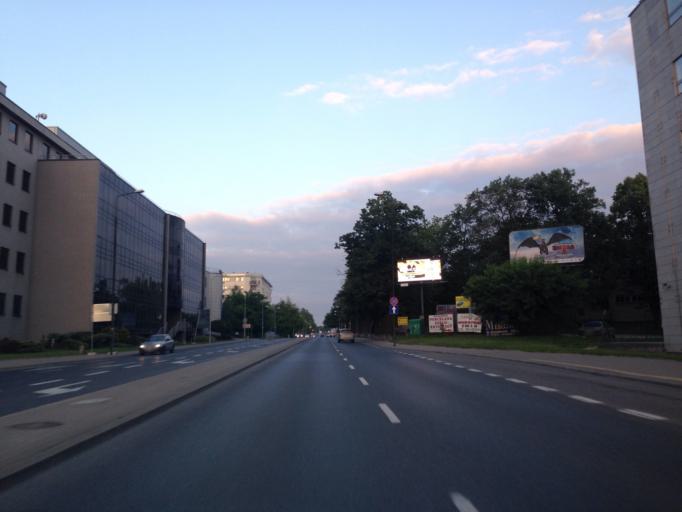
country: PL
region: Masovian Voivodeship
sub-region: Warszawa
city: Zoliborz
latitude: 52.2589
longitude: 20.9618
